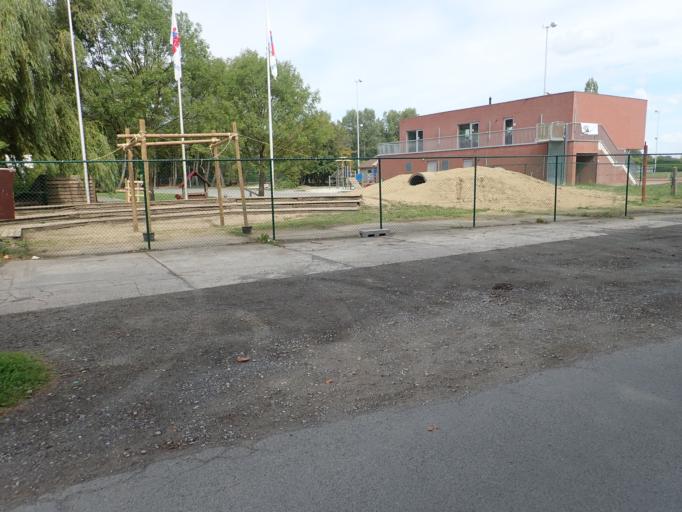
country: BE
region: Flanders
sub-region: Provincie Oost-Vlaanderen
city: Hamme
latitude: 51.1034
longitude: 4.1336
